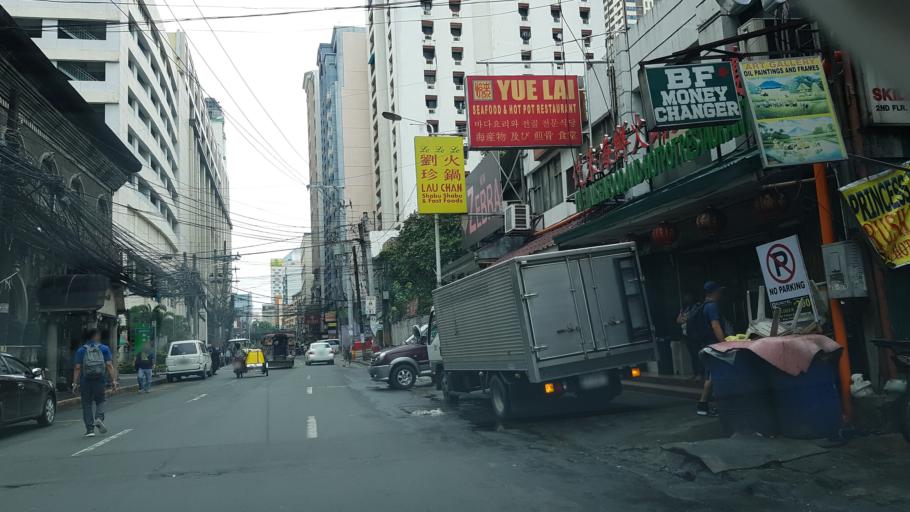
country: PH
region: Metro Manila
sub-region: City of Manila
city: Port Area
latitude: 14.5722
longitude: 120.9838
